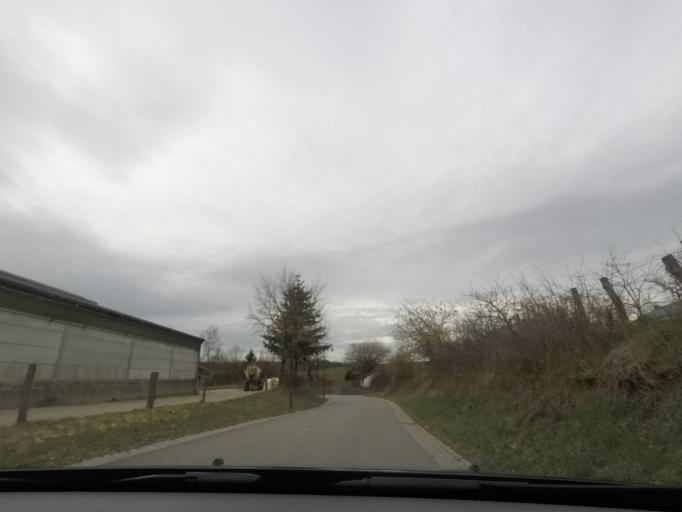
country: LU
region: Diekirch
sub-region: Canton de Clervaux
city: Wincrange
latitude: 50.0194
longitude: 5.9086
